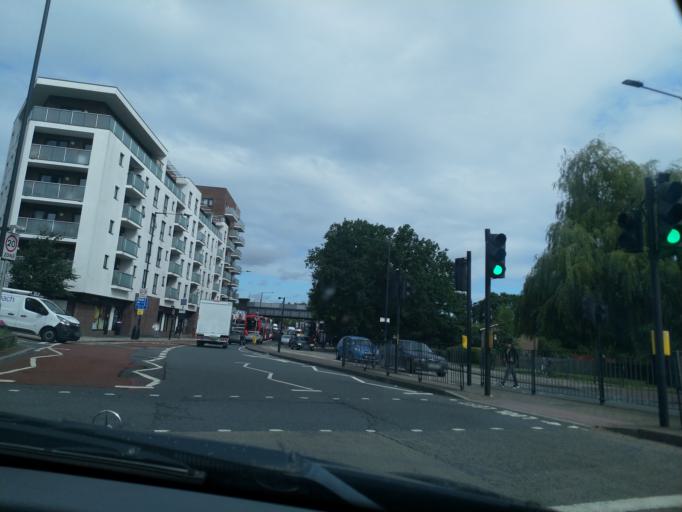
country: GB
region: England
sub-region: Greater London
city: Wembley
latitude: 51.5531
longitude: -0.3142
